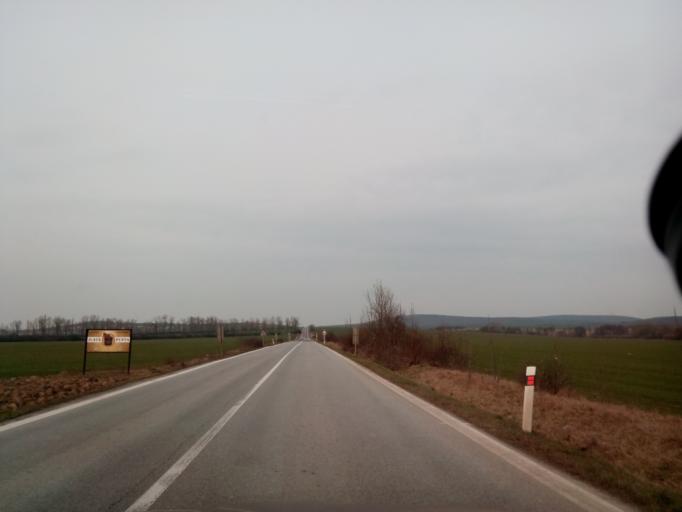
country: HU
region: Borsod-Abauj-Zemplen
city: Satoraljaujhely
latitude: 48.4688
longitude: 21.6391
